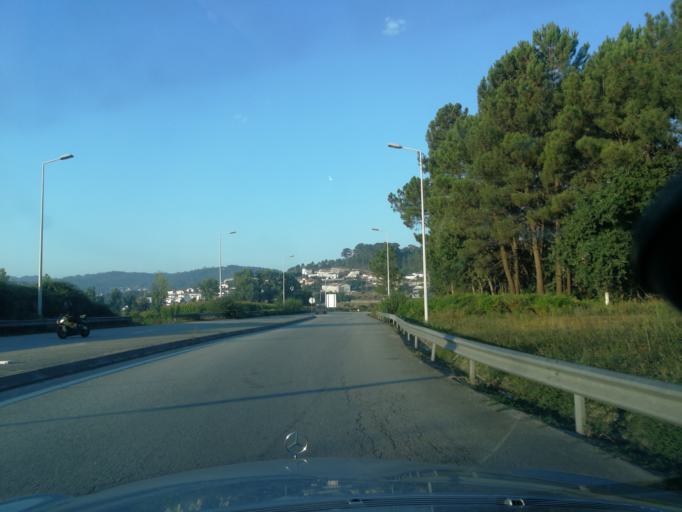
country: PT
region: Braga
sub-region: Braga
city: Braga
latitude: 41.5167
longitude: -8.4291
